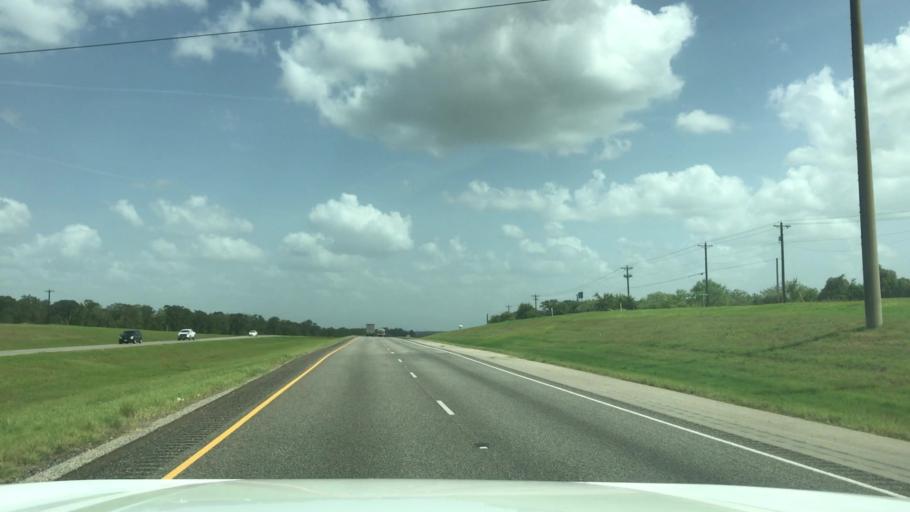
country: US
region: Texas
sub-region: Brazos County
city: Bryan
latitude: 30.7402
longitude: -96.4438
